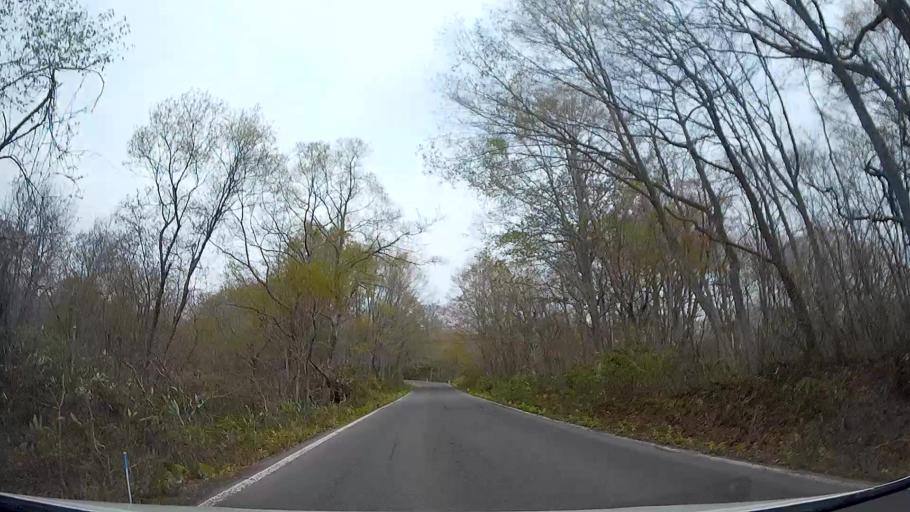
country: JP
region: Akita
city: Hanawa
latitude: 40.4030
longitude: 140.8659
